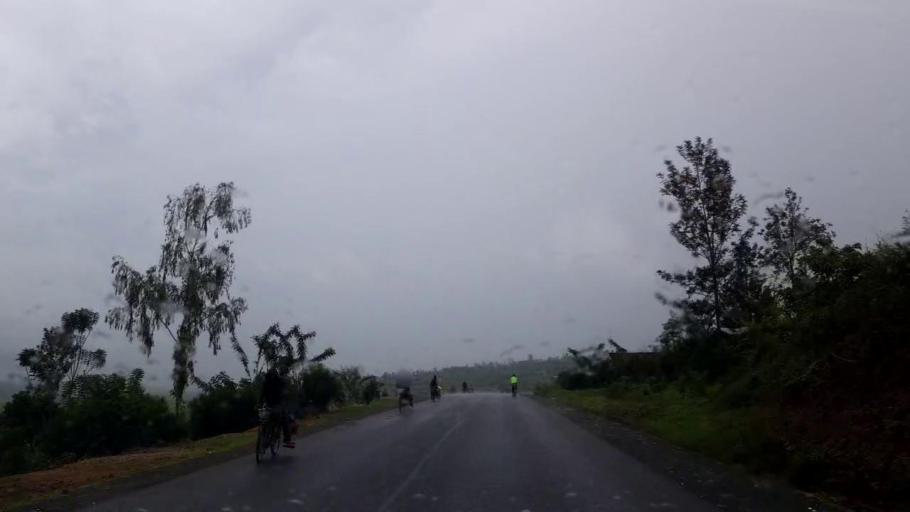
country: RW
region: Northern Province
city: Byumba
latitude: -1.4037
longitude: 30.2855
